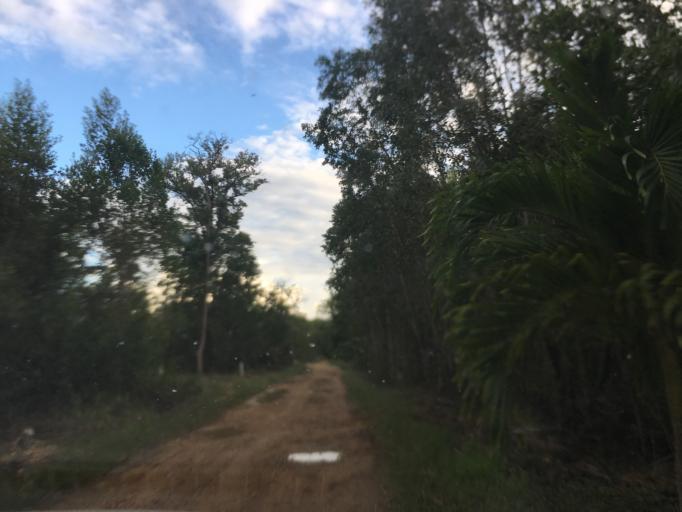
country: BZ
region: Stann Creek
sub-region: Dangriga
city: Dangriga
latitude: 16.8116
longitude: -88.2566
